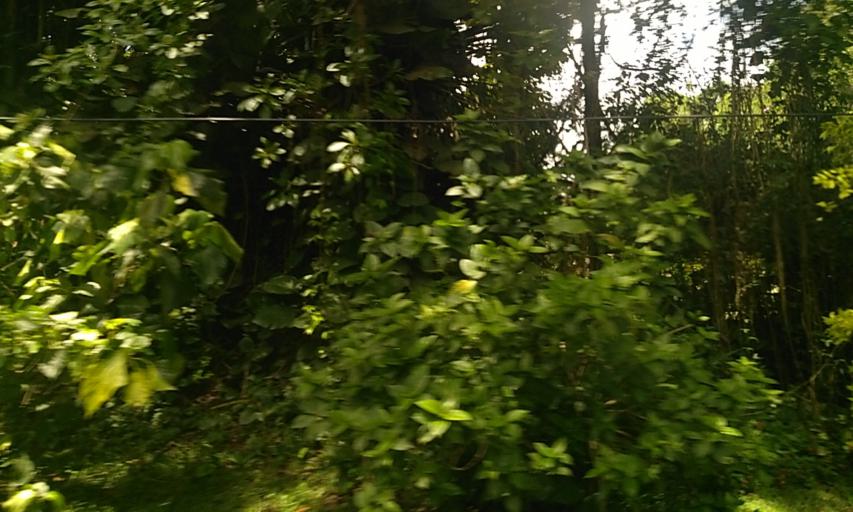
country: UG
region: Central Region
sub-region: Kampala District
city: Kampala
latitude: 0.3351
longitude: 32.5988
